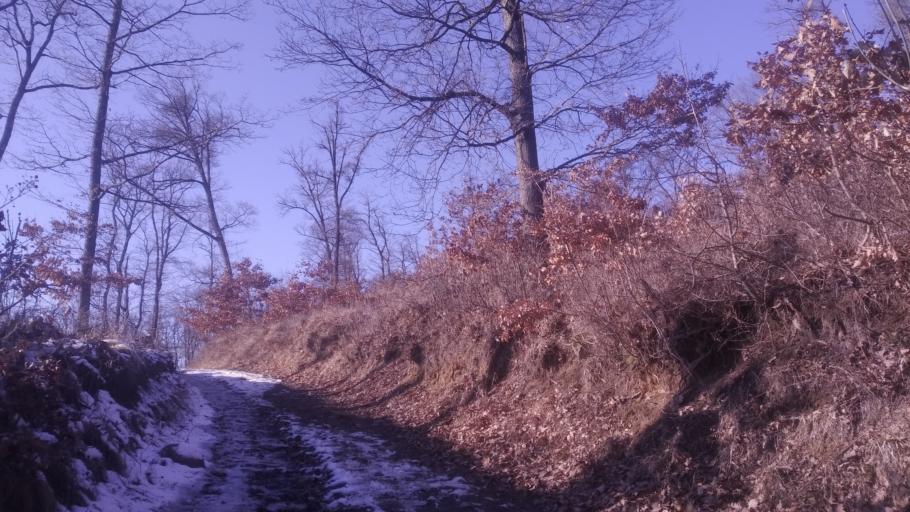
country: HU
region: Pest
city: Csobanka
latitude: 47.6794
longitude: 18.9610
